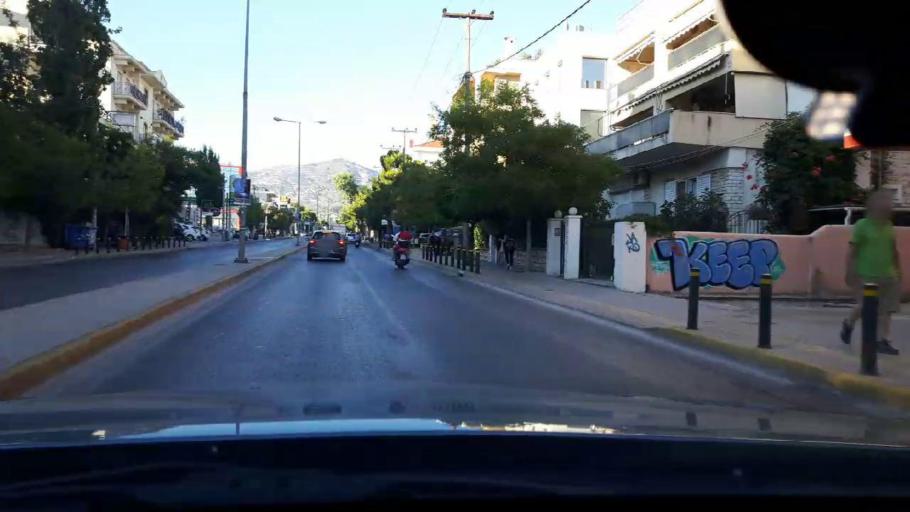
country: GR
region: Attica
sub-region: Nomarchia Athinas
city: Vrilissia
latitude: 38.0353
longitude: 23.8244
